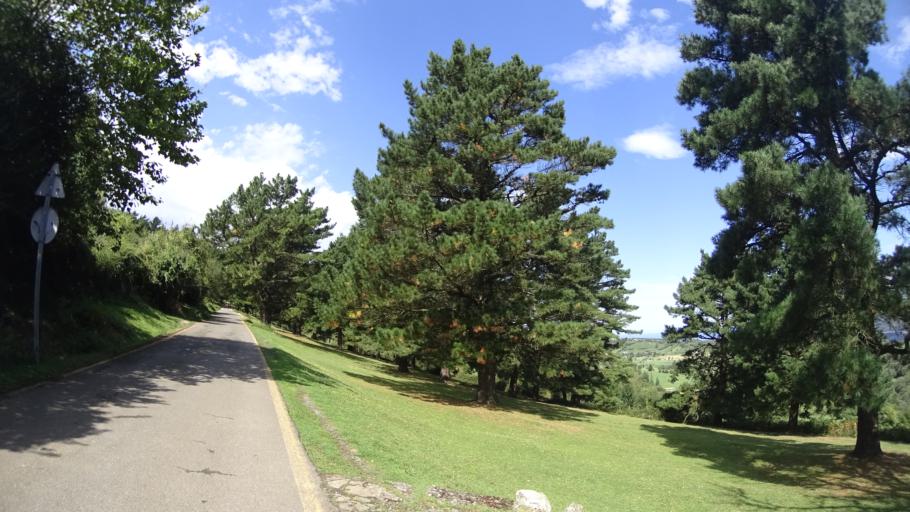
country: ES
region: Basque Country
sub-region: Bizkaia
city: Urtuella
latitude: 43.2835
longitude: -3.0607
